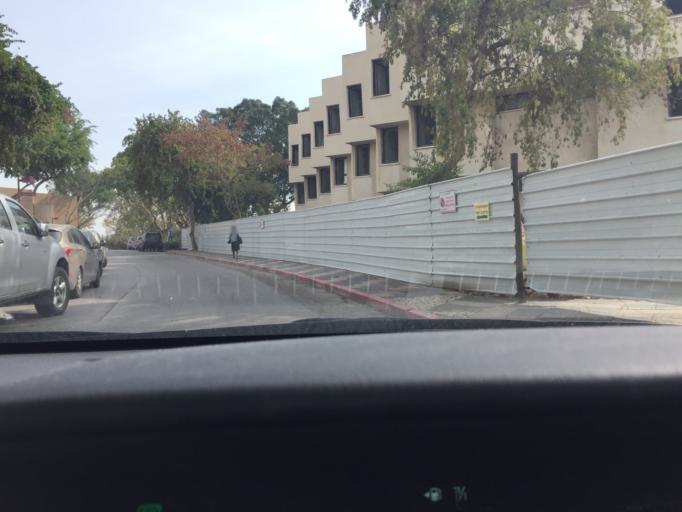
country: IL
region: Tel Aviv
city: Giv`at Shemu'el
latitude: 32.0666
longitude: 34.8407
